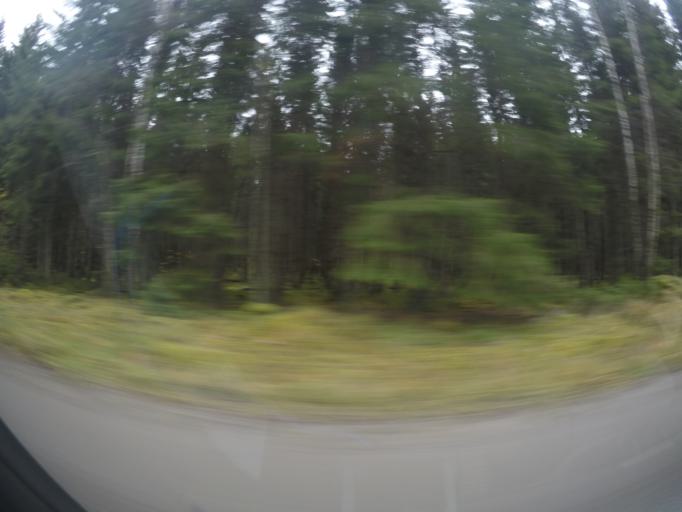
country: SE
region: Vaestmanland
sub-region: Surahammars Kommun
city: Ramnas
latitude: 59.7119
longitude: 16.0925
